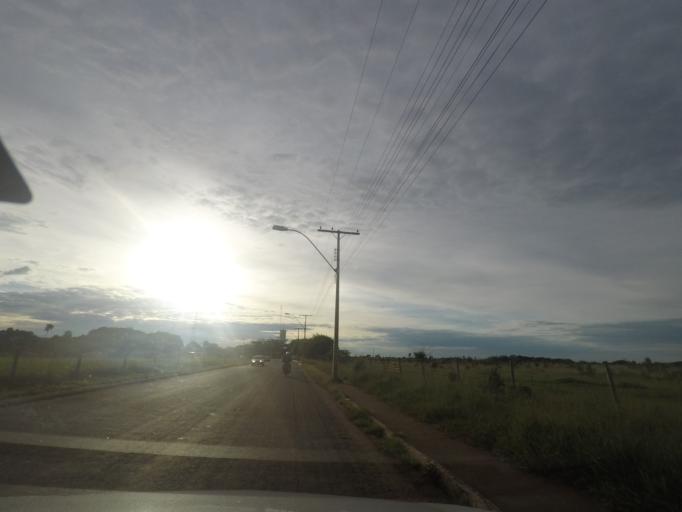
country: BR
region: Goias
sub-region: Trindade
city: Trindade
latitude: -16.7201
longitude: -49.4373
